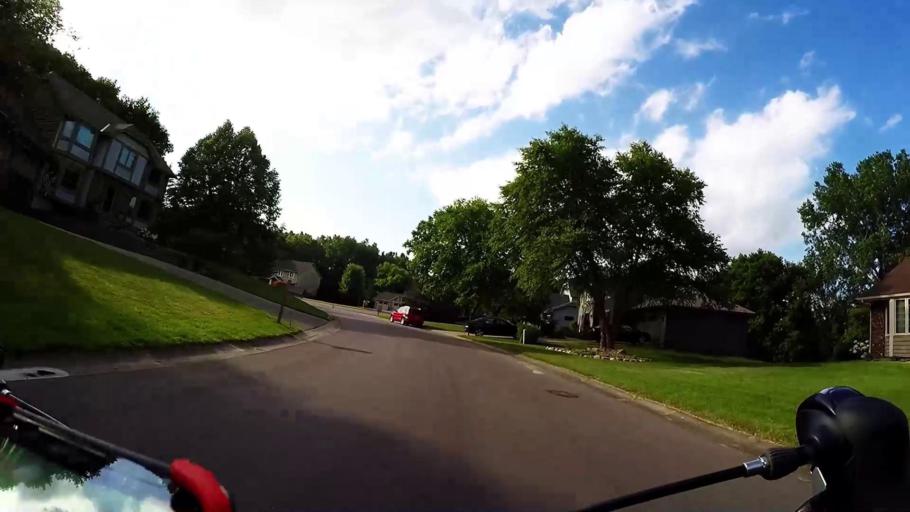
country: US
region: Minnesota
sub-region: Hennepin County
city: Minnetonka
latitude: 44.8878
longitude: -93.4871
